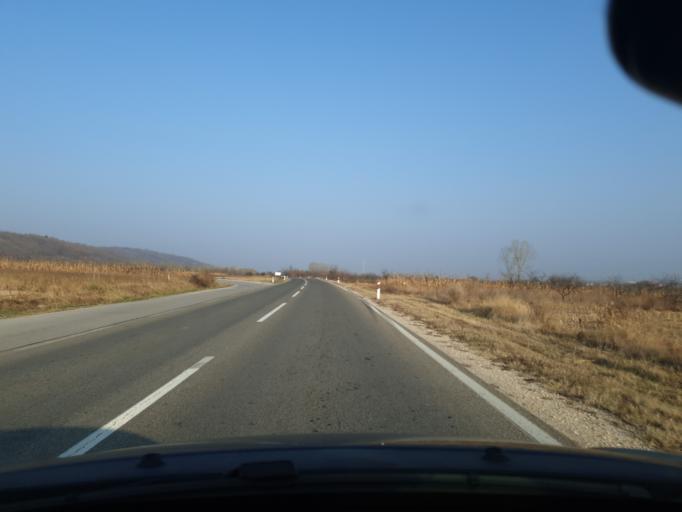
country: RS
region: Central Serbia
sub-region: Jablanicki Okrug
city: Leskovac
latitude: 42.9518
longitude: 21.9901
